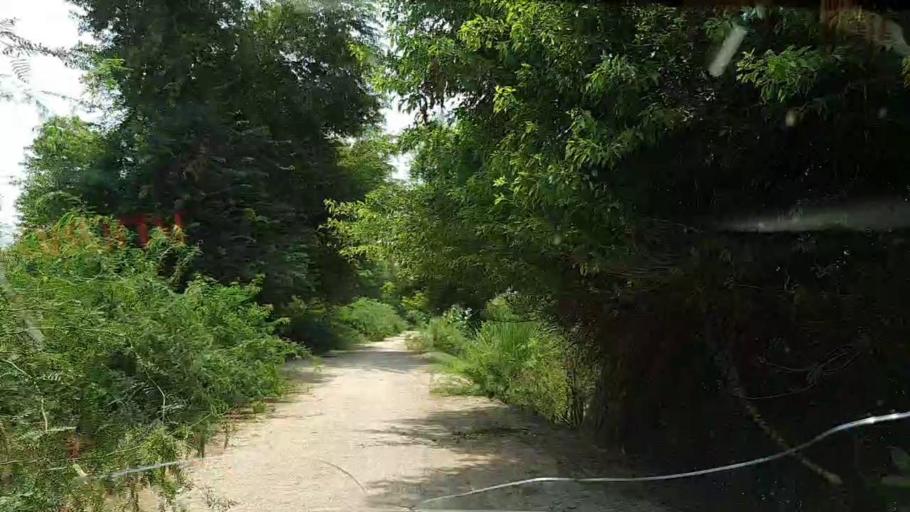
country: PK
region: Sindh
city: Adilpur
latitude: 27.8762
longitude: 69.2602
